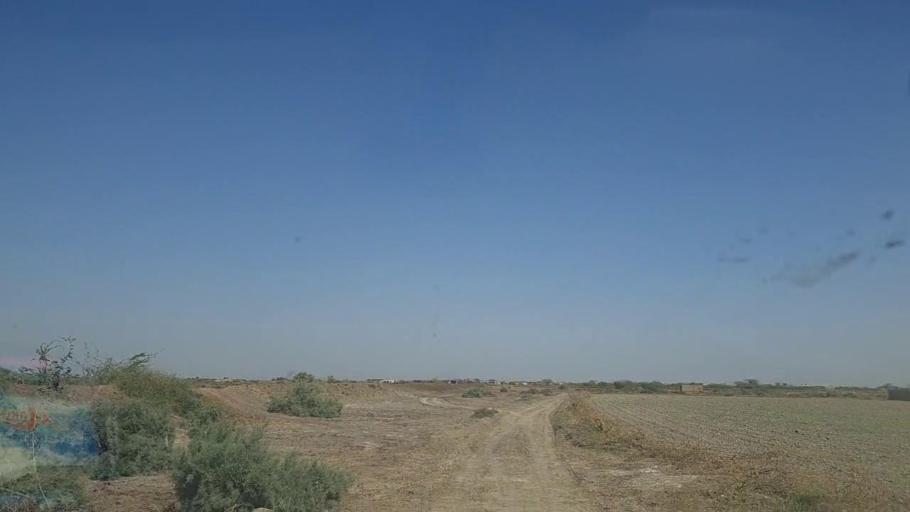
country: PK
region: Sindh
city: Chuhar Jamali
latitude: 24.2722
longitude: 67.7539
